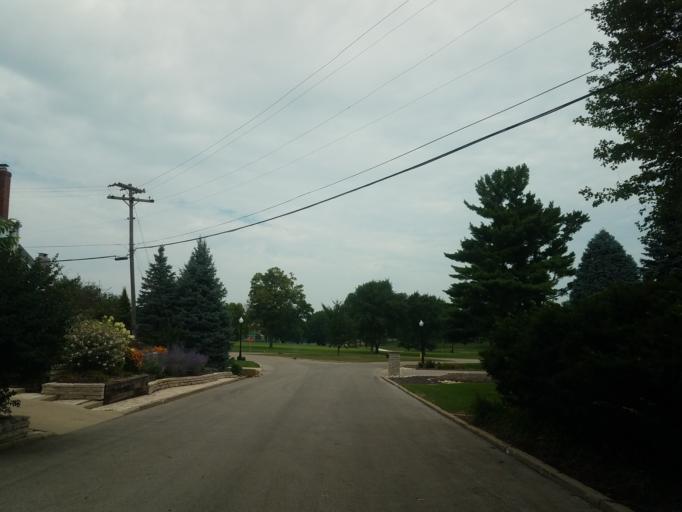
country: US
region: Illinois
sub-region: McLean County
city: Bloomington
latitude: 40.4811
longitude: -88.9727
